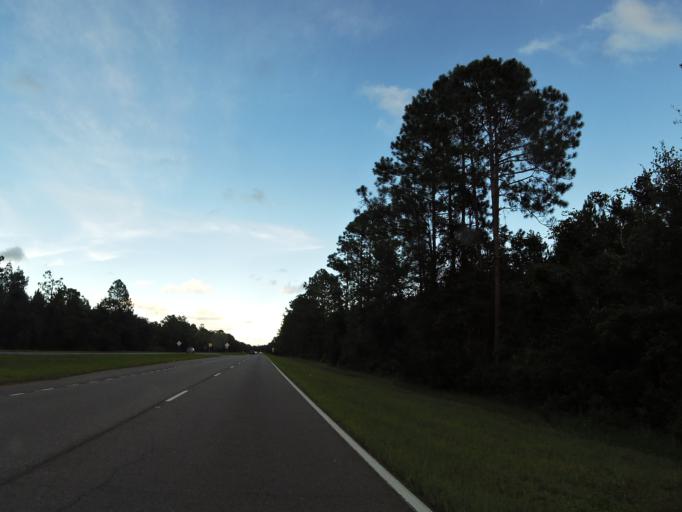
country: US
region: Georgia
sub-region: Camden County
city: Kingsland
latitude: 30.7604
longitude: -81.6449
